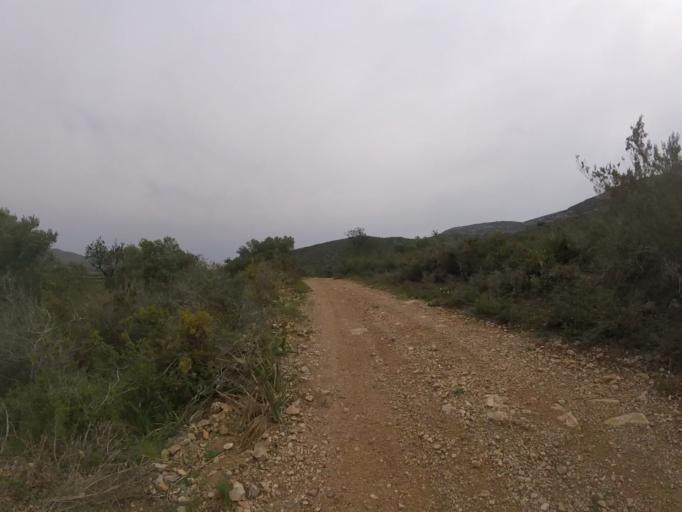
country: ES
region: Valencia
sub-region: Provincia de Castello
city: Santa Magdalena de Pulpis
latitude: 40.3691
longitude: 0.3312
